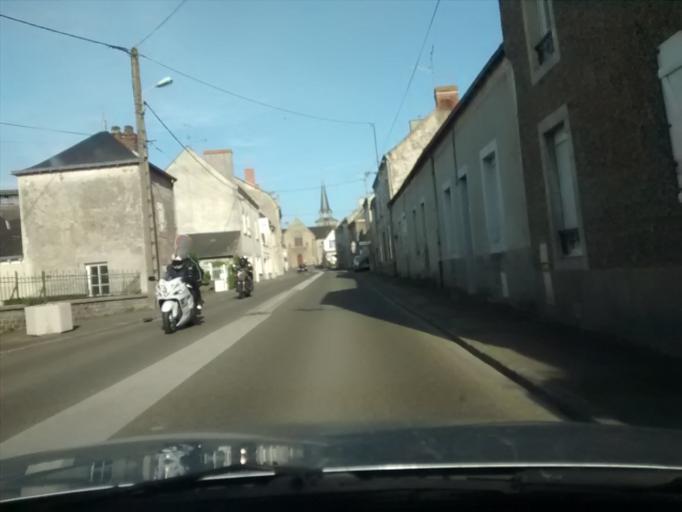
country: FR
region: Pays de la Loire
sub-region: Departement de la Mayenne
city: Vaiges
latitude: 48.0414
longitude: -0.4798
